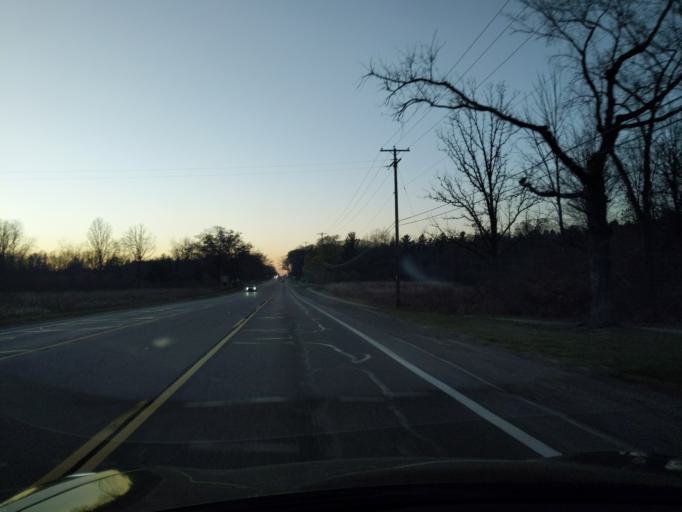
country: US
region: Michigan
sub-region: Ingham County
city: Haslett
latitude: 42.7105
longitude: -84.3684
